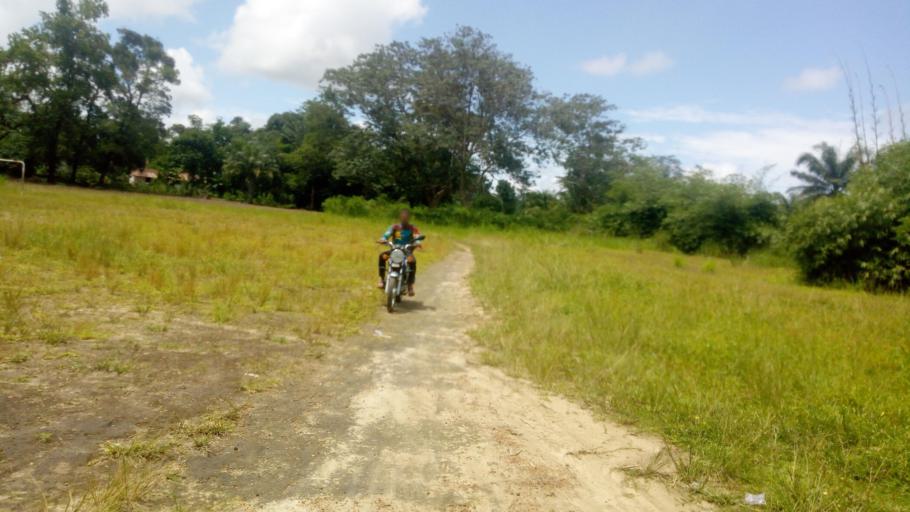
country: SL
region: Northern Province
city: Magburaka
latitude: 8.7193
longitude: -11.9468
